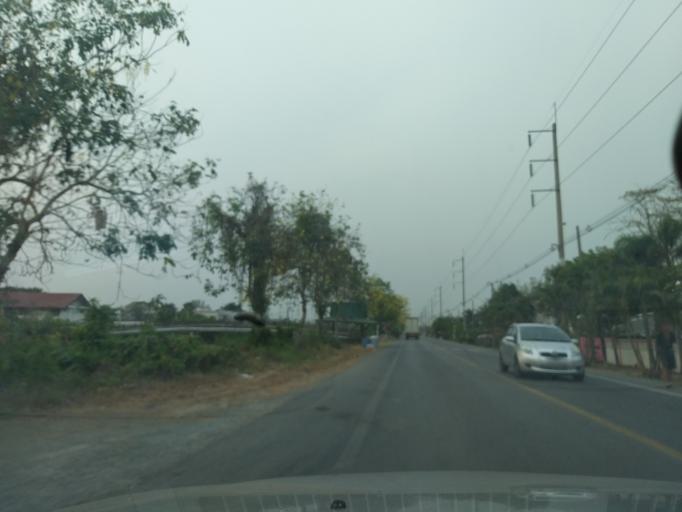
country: TH
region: Pathum Thani
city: Ban Lam Luk Ka
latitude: 13.9901
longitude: 100.8952
